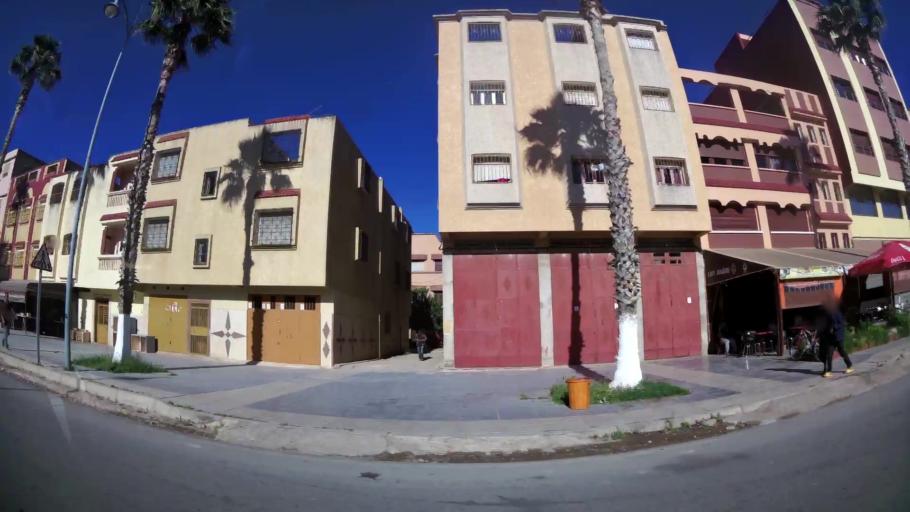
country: MA
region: Oriental
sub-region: Berkane-Taourirt
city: Ahfir
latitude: 34.9554
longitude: -2.1070
